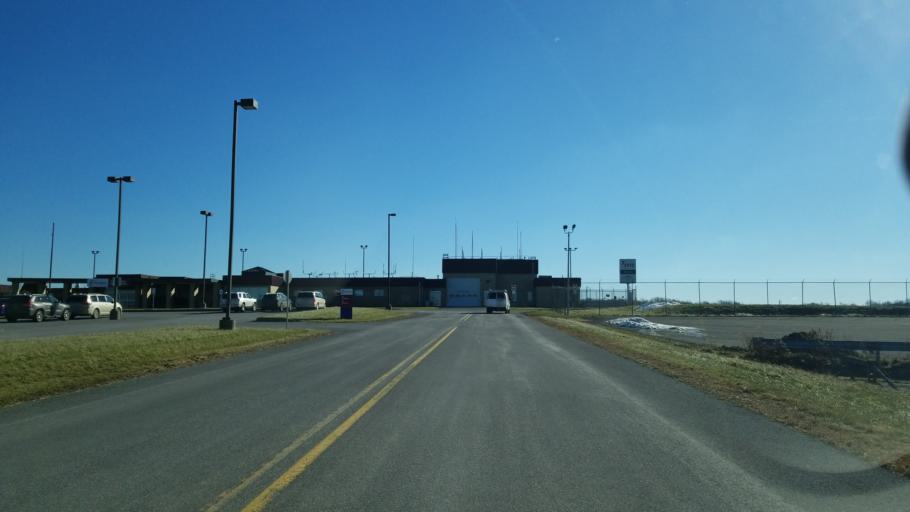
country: US
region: Pennsylvania
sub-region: Jefferson County
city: Reynoldsville
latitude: 41.1837
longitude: -78.8937
